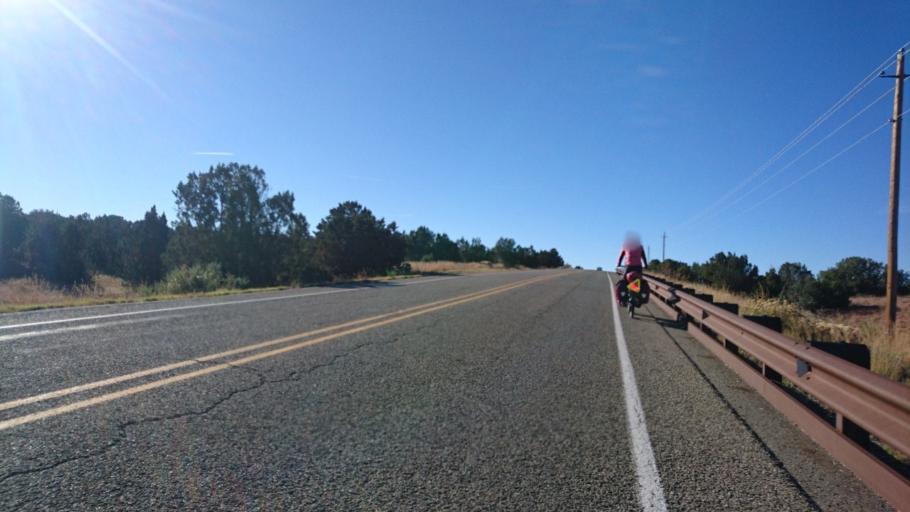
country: US
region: New Mexico
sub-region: Santa Fe County
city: La Cienega
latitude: 35.4731
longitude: -106.0693
